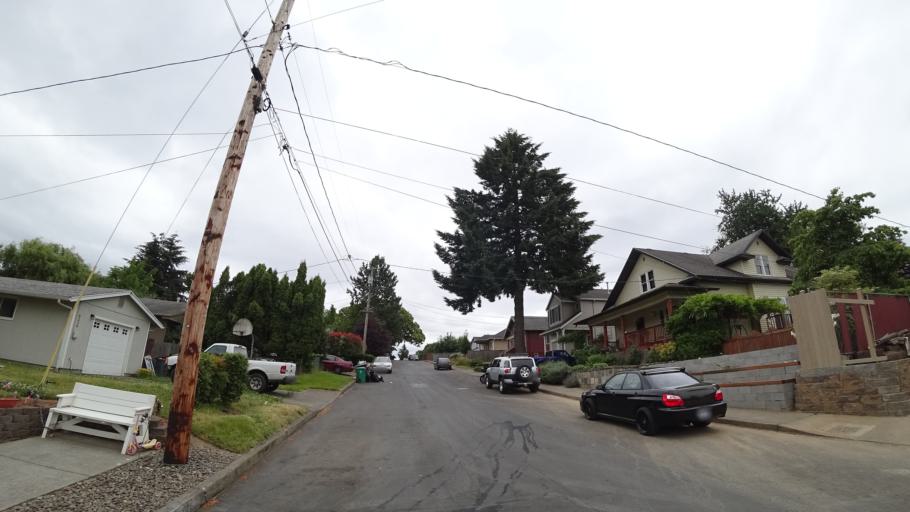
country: US
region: Washington
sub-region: Clark County
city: Vancouver
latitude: 45.5897
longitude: -122.7023
